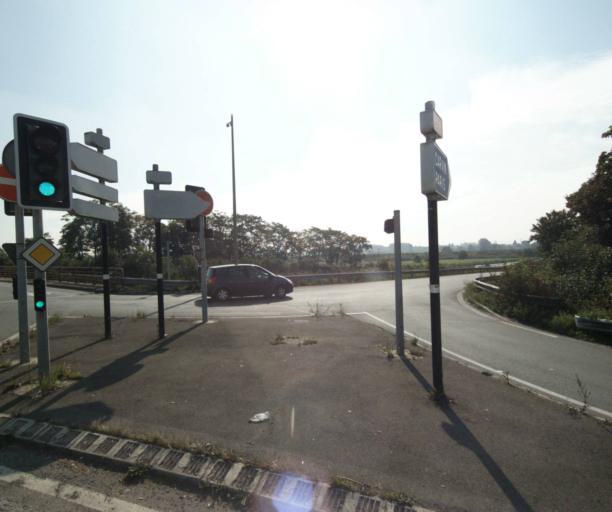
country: FR
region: Nord-Pas-de-Calais
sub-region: Departement du Nord
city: Attiches
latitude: 50.5449
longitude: 3.0552
